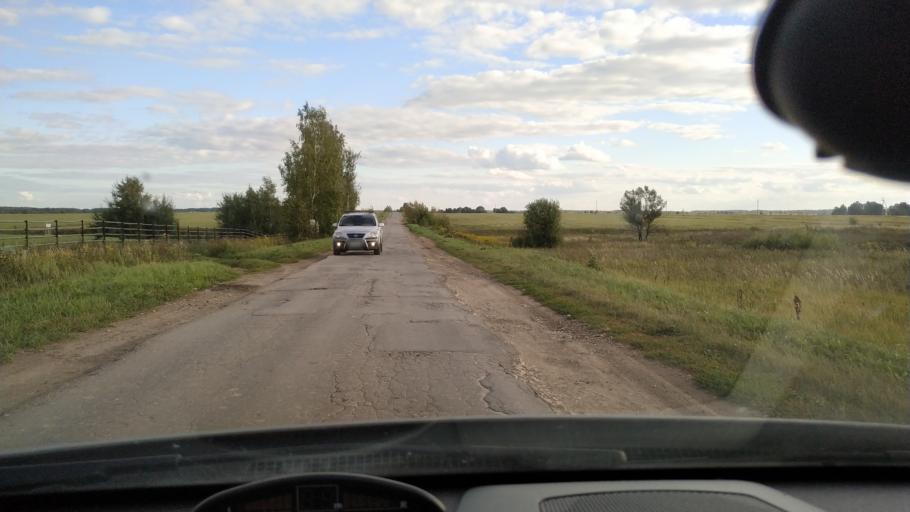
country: RU
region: Rjazan
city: Polyany
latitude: 54.5741
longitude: 39.8614
